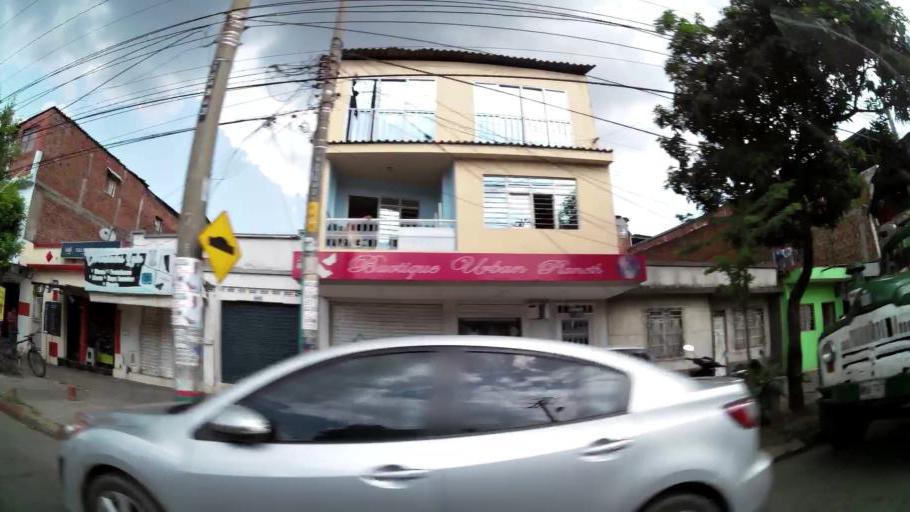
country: CO
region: Valle del Cauca
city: Cali
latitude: 3.4741
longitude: -76.5098
